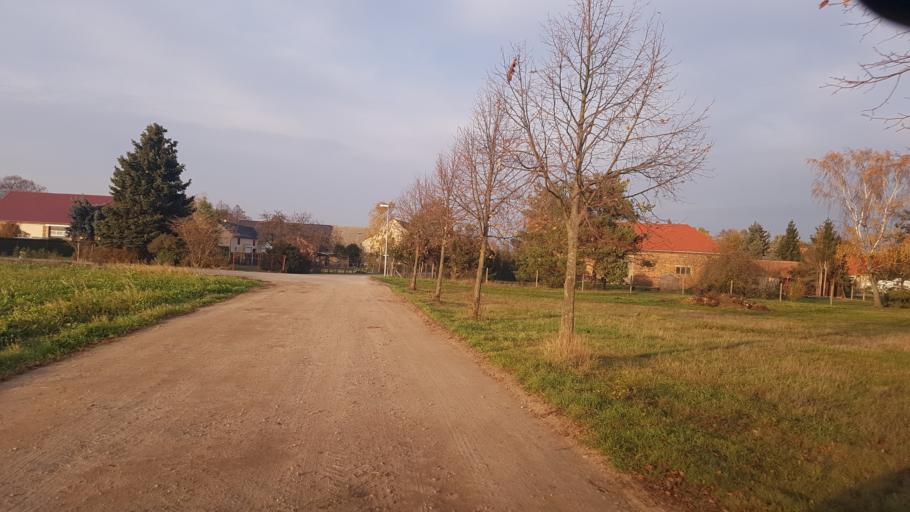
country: DE
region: Brandenburg
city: Schonewalde
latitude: 51.6562
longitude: 13.5983
